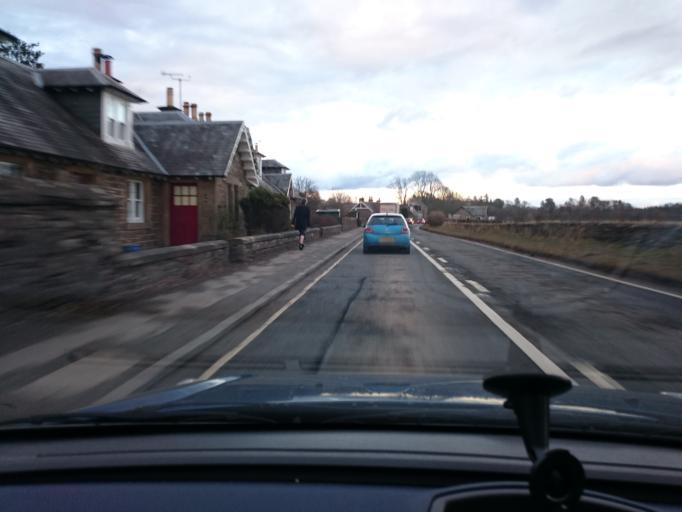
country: GB
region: Scotland
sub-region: Stirling
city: Doune
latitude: 56.2008
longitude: -4.0802
